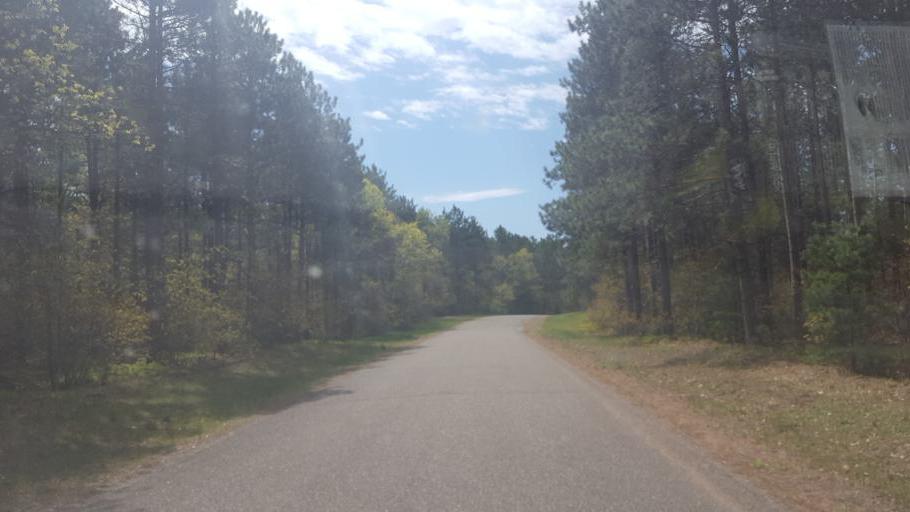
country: US
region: Wisconsin
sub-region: Clark County
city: Neillsville
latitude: 44.3393
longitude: -90.4977
